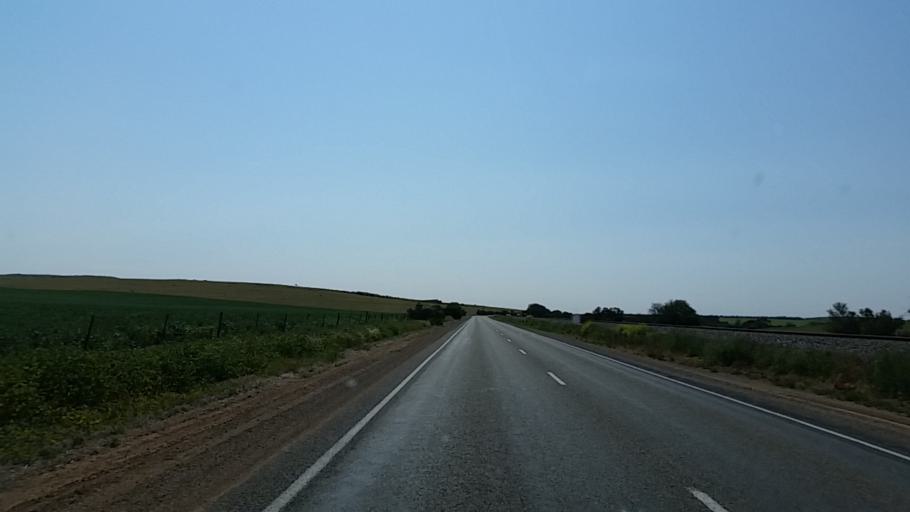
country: AU
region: South Australia
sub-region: Port Pirie City and Dists
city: Crystal Brook
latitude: -33.2456
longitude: 138.3715
